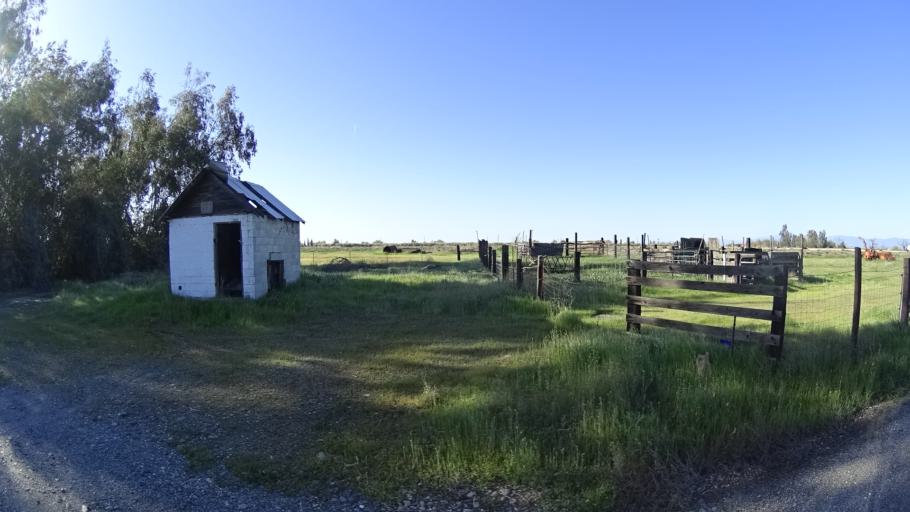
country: US
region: California
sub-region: Glenn County
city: Orland
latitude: 39.7550
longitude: -122.2311
